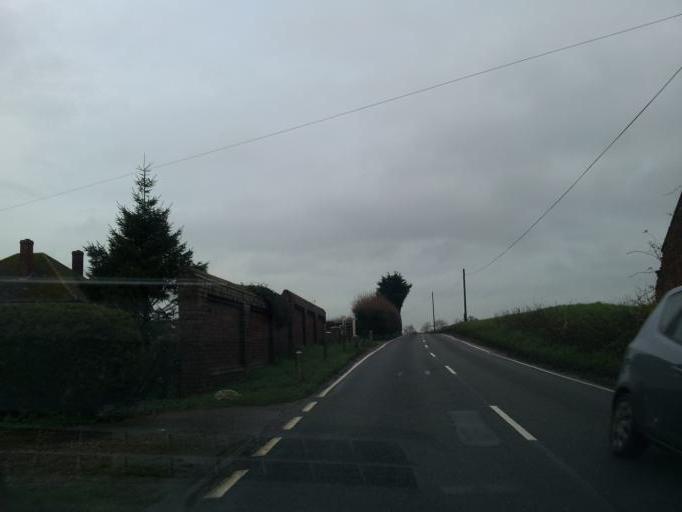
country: GB
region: England
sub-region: Norfolk
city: Acle
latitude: 52.6652
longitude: 1.5880
